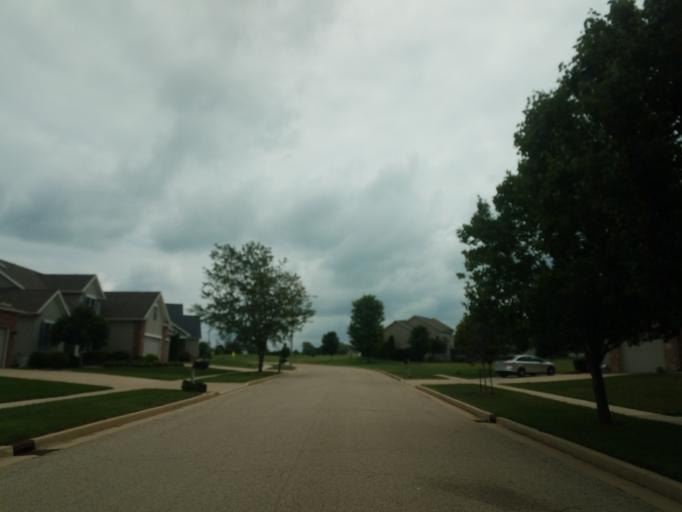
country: US
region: Illinois
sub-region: McLean County
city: Bloomington
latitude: 40.4421
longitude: -89.0389
